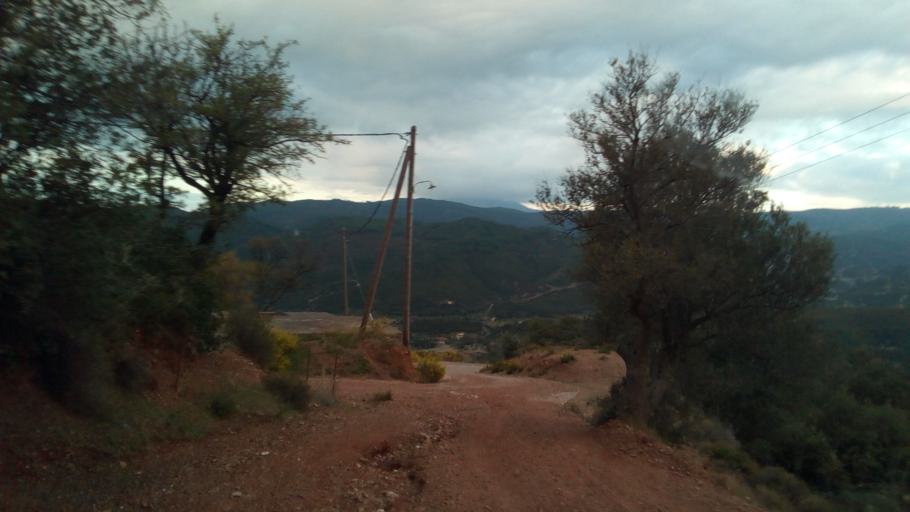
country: GR
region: West Greece
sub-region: Nomos Aitolias kai Akarnanias
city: Nafpaktos
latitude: 38.4066
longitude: 21.8030
